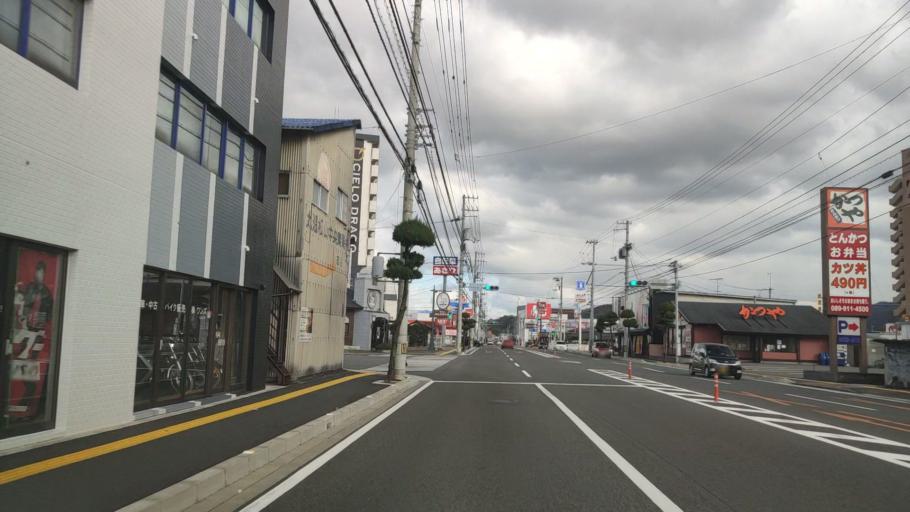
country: JP
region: Ehime
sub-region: Shikoku-chuo Shi
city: Matsuyama
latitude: 33.8616
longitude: 132.7496
